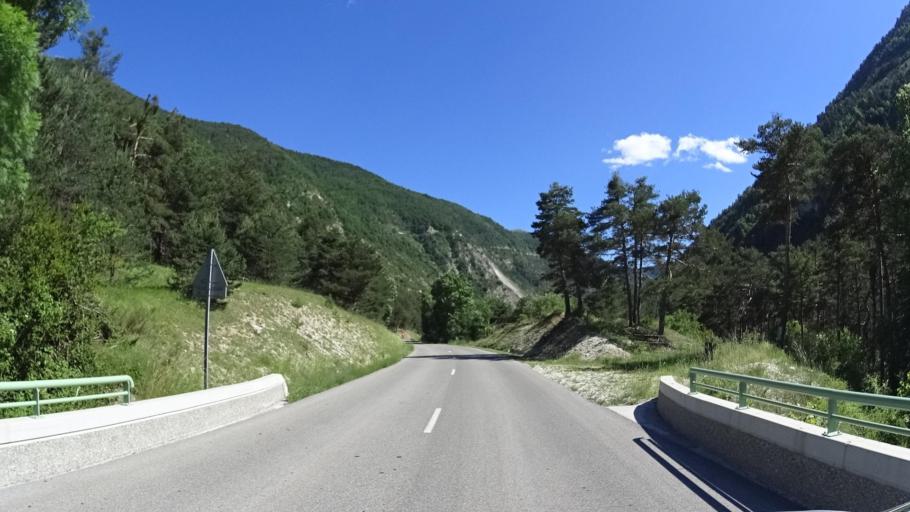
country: FR
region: Provence-Alpes-Cote d'Azur
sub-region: Departement des Alpes-de-Haute-Provence
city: Annot
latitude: 44.0702
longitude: 6.5731
